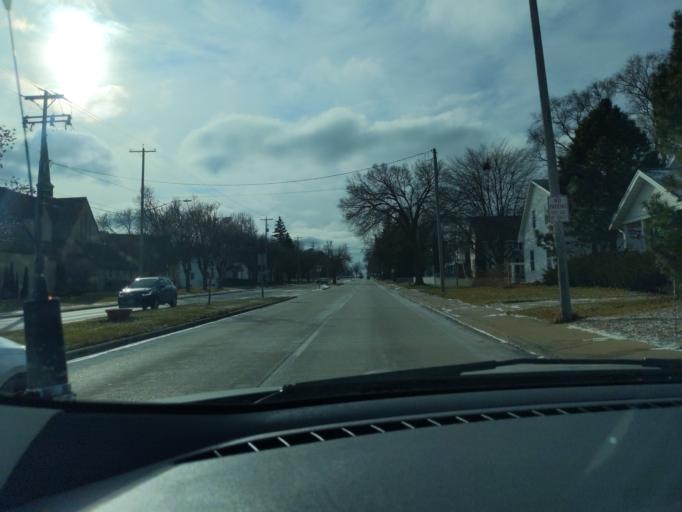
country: US
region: Wisconsin
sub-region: Brown County
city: Allouez
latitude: 44.4799
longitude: -88.0250
